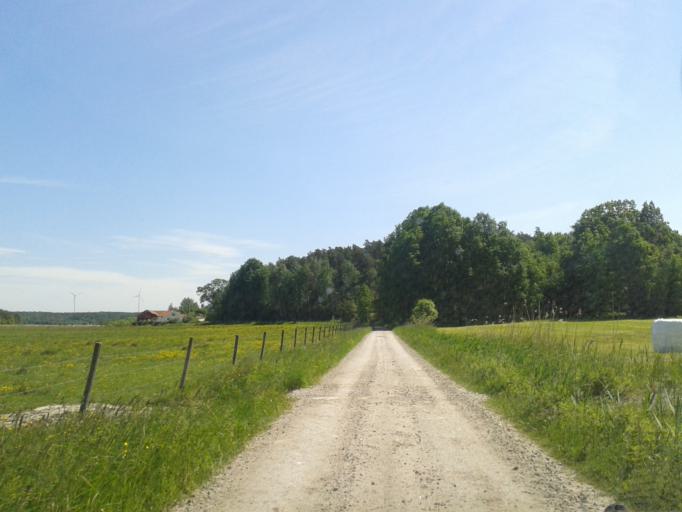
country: SE
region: Vaestra Goetaland
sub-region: Stromstads Kommun
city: Stroemstad
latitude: 58.8630
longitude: 11.2164
